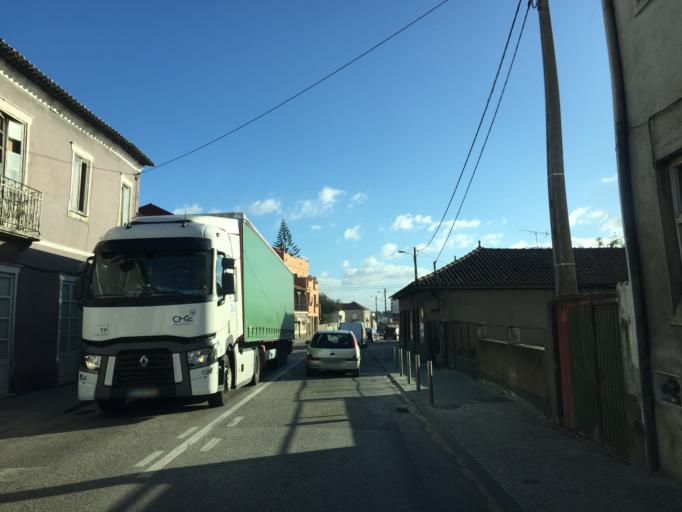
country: PT
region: Leiria
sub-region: Leiria
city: Monte Redondo
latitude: 39.9467
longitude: -8.7847
